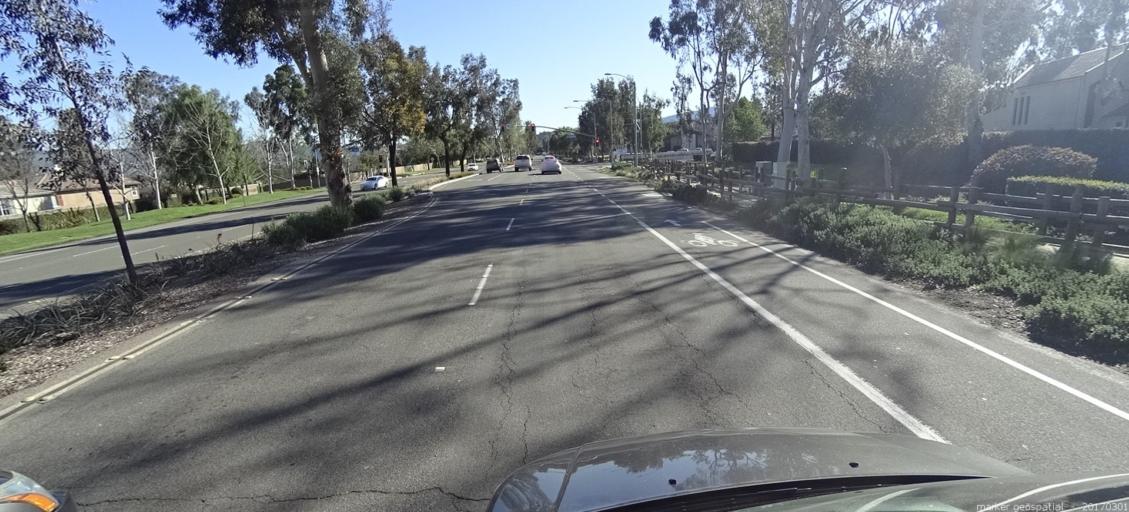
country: US
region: California
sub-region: Orange County
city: Yorba Linda
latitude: 33.8523
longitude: -117.7848
